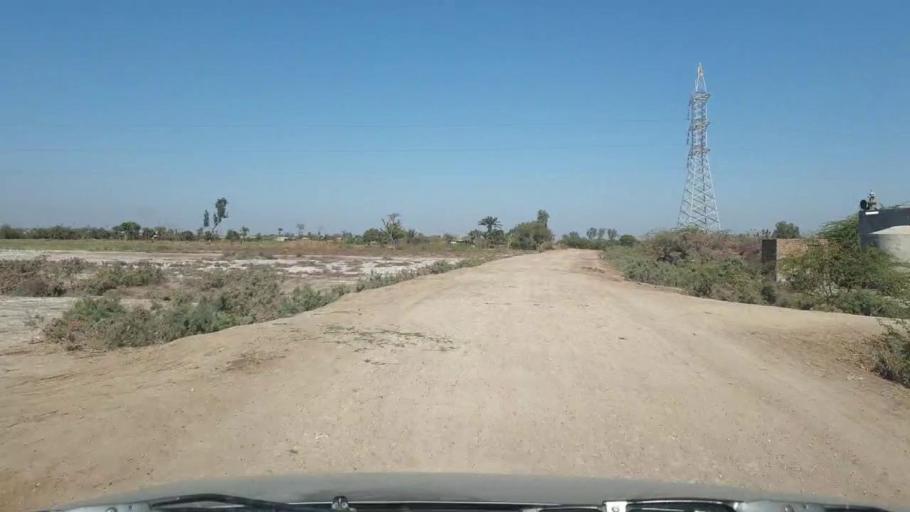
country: PK
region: Sindh
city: Mirwah Gorchani
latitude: 25.3128
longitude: 69.1283
